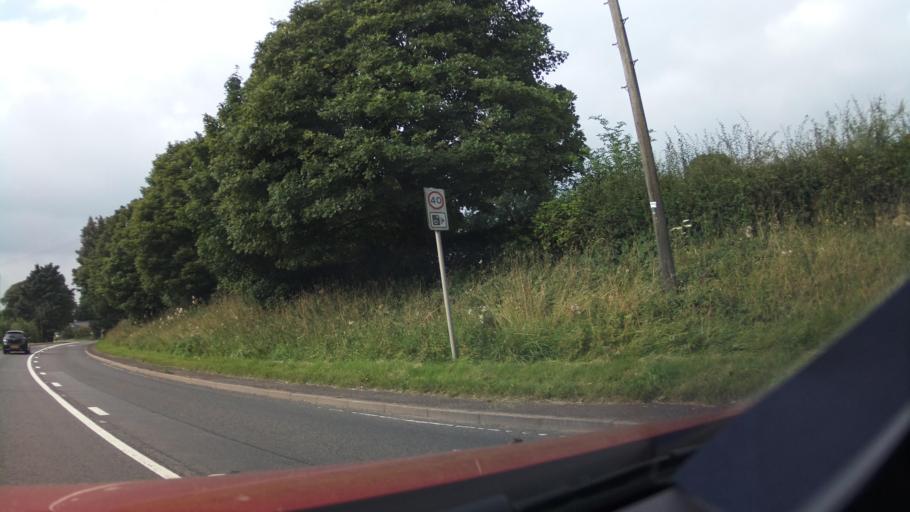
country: GB
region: England
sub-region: Staffordshire
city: Mayfield
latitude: 53.0301
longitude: -1.8008
